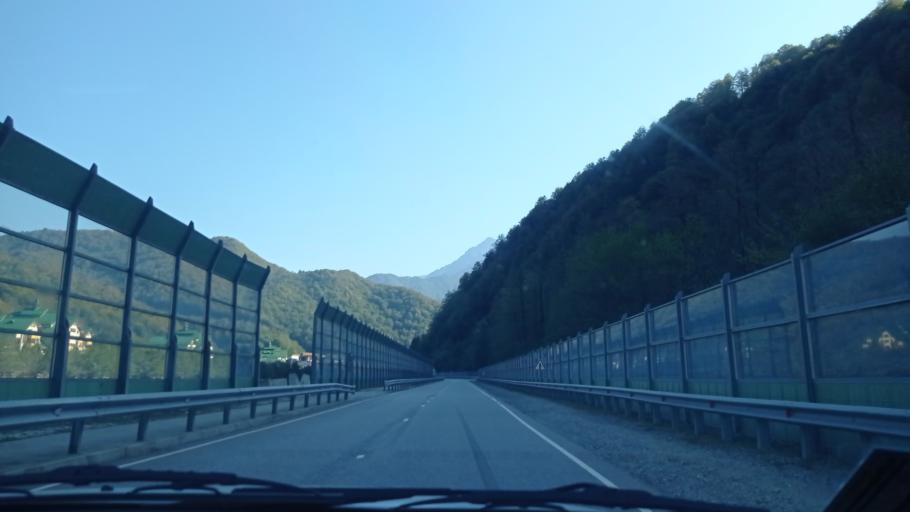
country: RU
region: Krasnodarskiy
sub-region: Sochi City
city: Krasnaya Polyana
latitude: 43.6935
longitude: 40.2696
